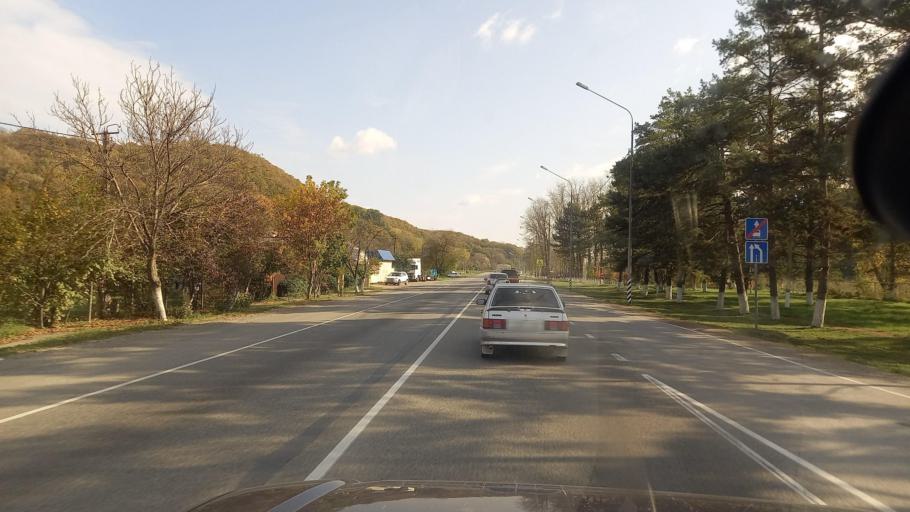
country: RU
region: Krasnodarskiy
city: Krymsk
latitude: 44.8693
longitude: 37.8885
